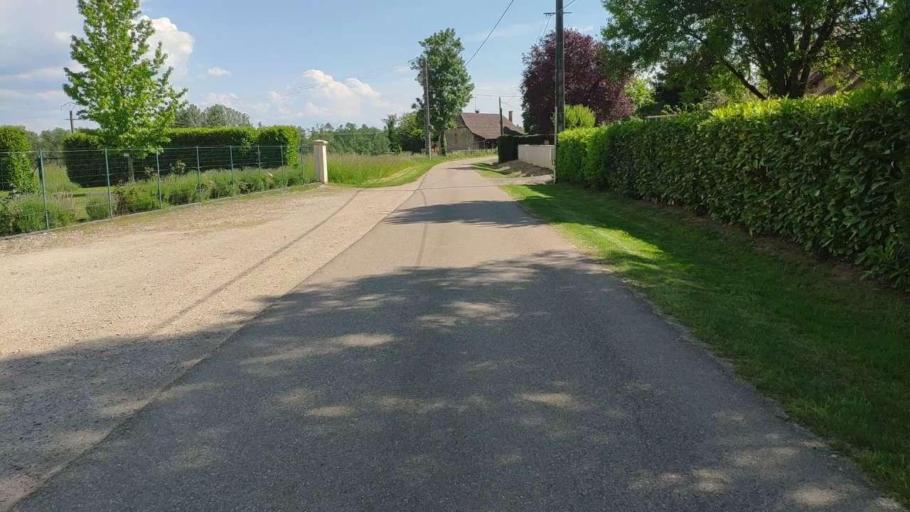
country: FR
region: Franche-Comte
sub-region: Departement du Jura
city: Bletterans
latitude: 46.8010
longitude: 5.4091
